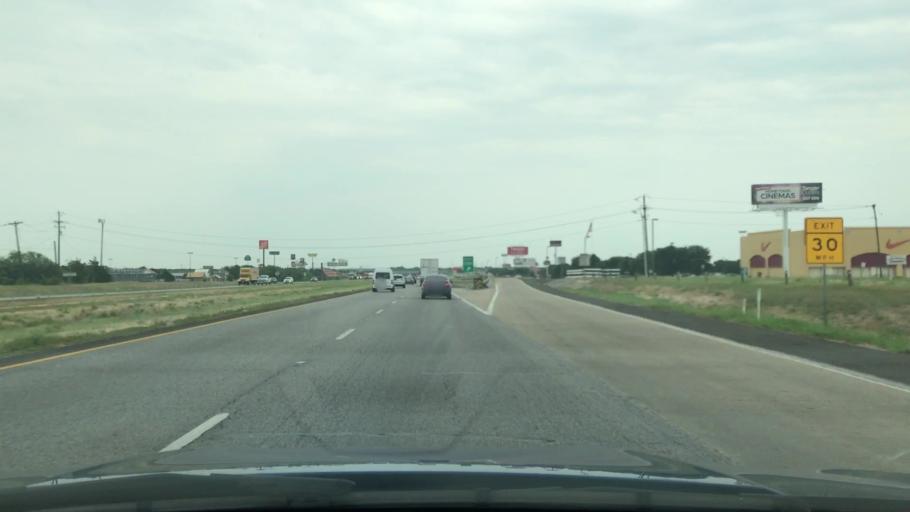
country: US
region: Texas
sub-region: Kaufman County
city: Terrell
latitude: 32.7053
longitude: -96.2855
